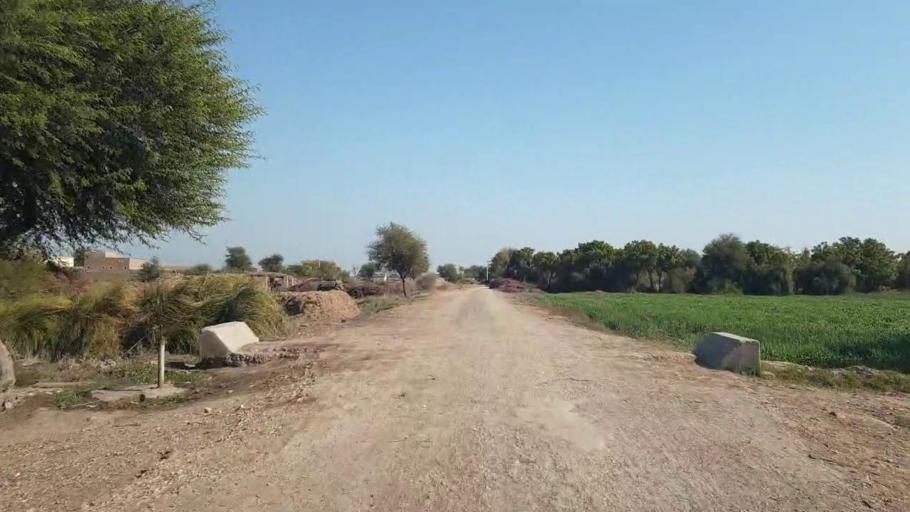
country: PK
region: Sindh
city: Shahdadpur
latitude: 25.9681
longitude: 68.6529
